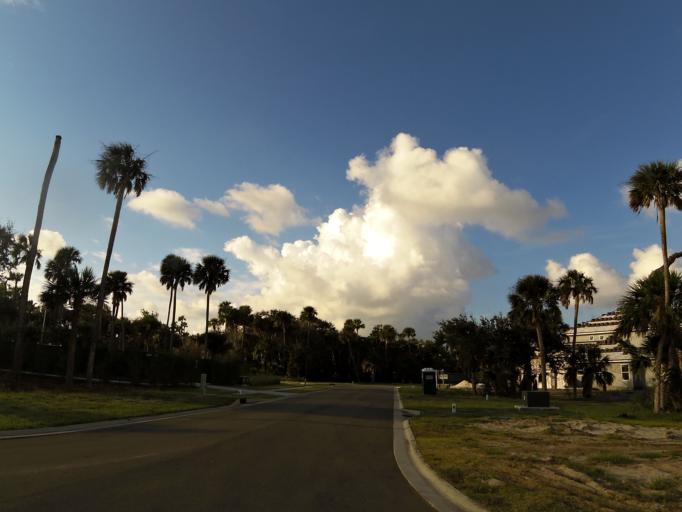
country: US
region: Florida
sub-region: Saint Johns County
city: Sawgrass
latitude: 30.1703
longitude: -81.3619
